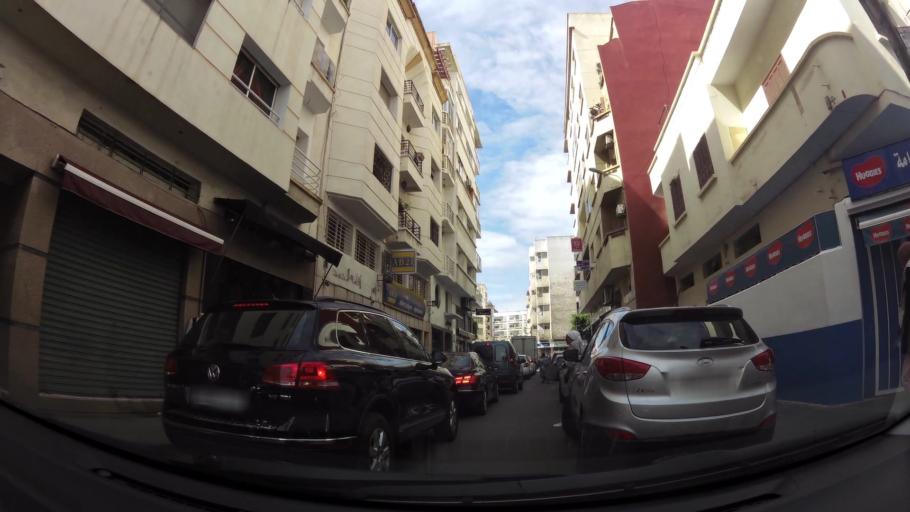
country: MA
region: Grand Casablanca
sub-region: Casablanca
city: Casablanca
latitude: 33.5822
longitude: -7.6388
